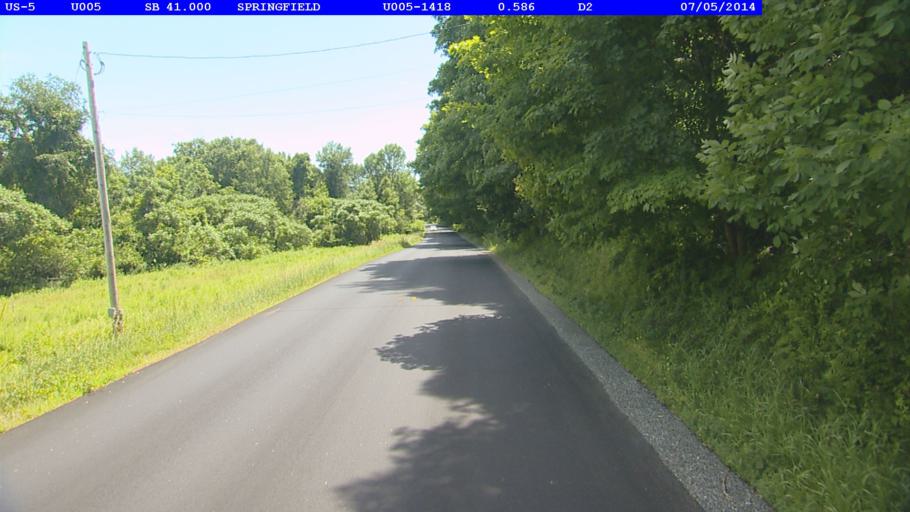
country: US
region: New Hampshire
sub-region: Sullivan County
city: Charlestown
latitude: 43.2416
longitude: -72.4397
